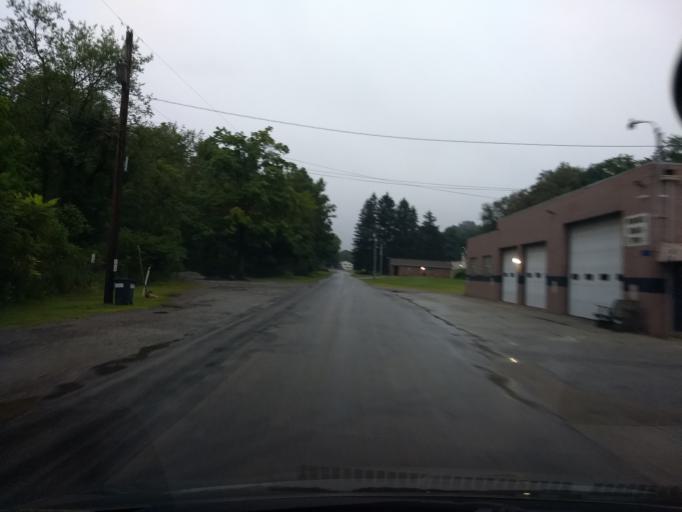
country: US
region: Pennsylvania
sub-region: Westmoreland County
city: Greensburg
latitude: 40.3544
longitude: -79.5227
